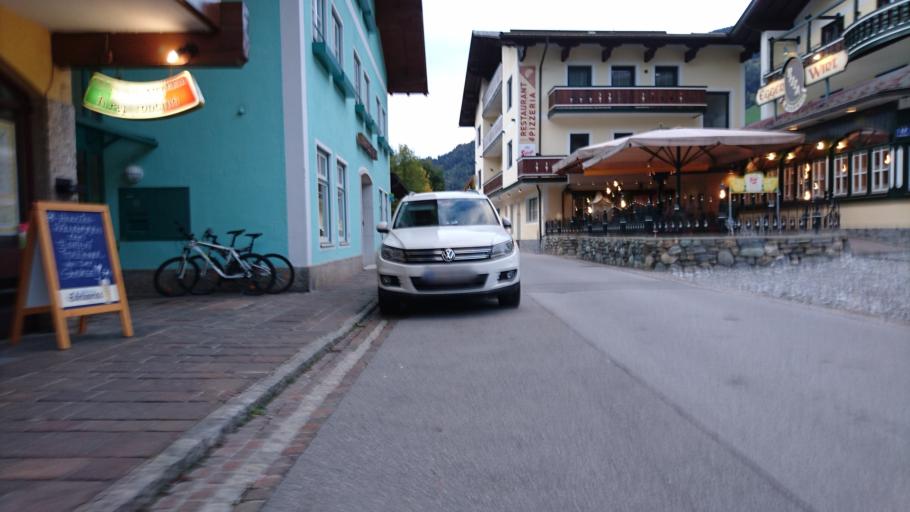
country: AT
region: Salzburg
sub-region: Politischer Bezirk Sankt Johann im Pongau
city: Dorfgastein
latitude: 47.2424
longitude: 13.1054
